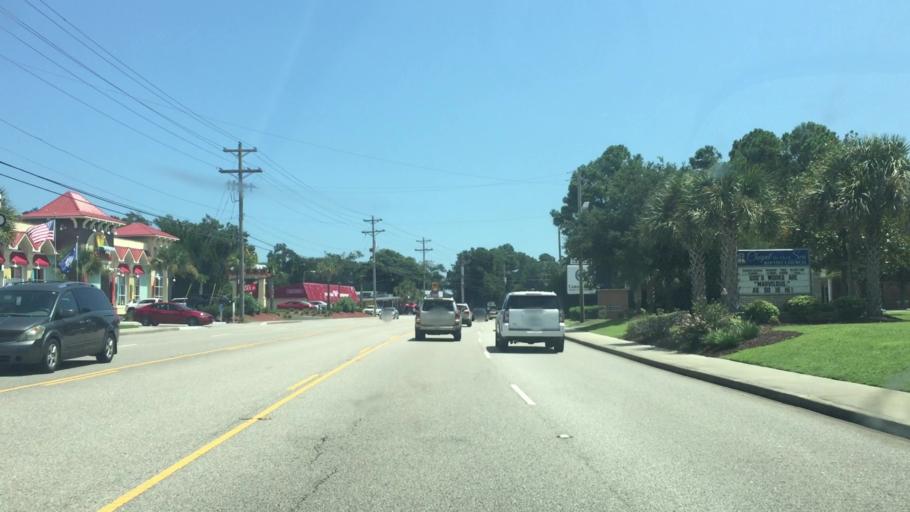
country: US
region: South Carolina
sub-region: Horry County
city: North Myrtle Beach
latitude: 33.8408
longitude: -78.6463
